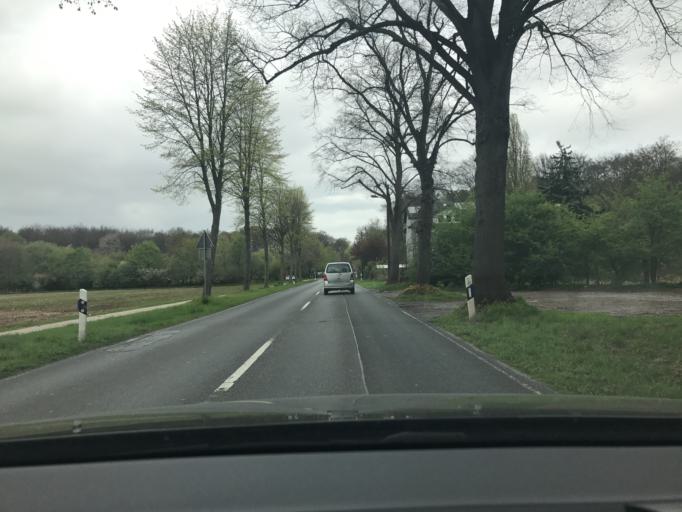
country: DE
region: North Rhine-Westphalia
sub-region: Regierungsbezirk Dusseldorf
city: Willich
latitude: 51.2967
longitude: 6.5325
